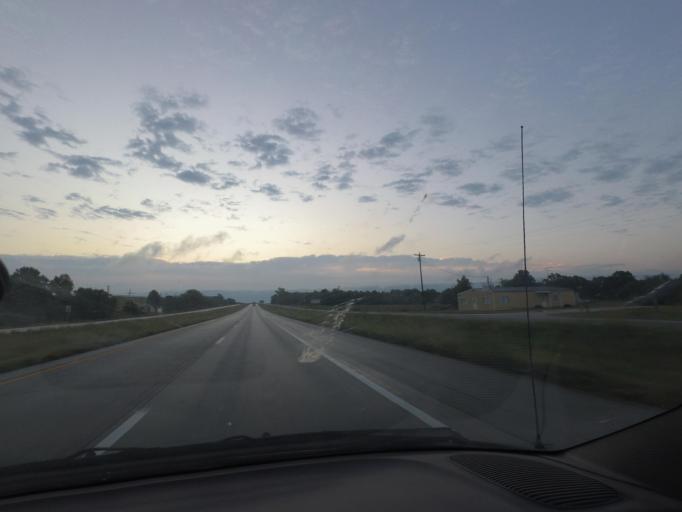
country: US
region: Missouri
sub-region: Macon County
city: Macon
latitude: 39.7489
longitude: -92.5166
